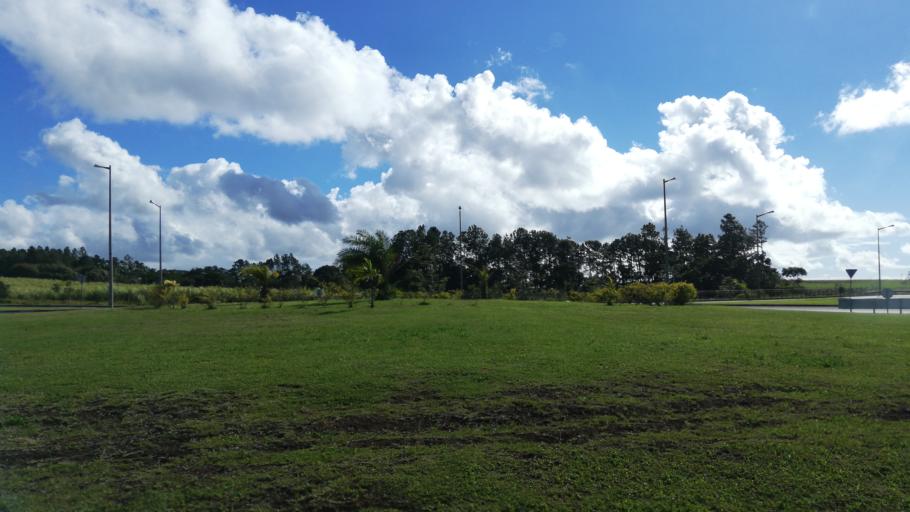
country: MU
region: Moka
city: Providence
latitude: -20.2466
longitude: 57.6048
